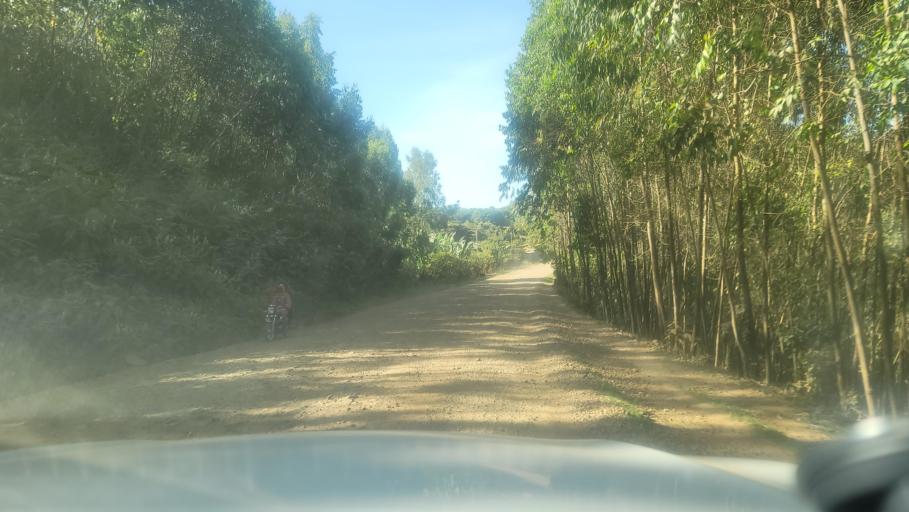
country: ET
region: Oromiya
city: Agaro
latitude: 7.8017
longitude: 36.4996
